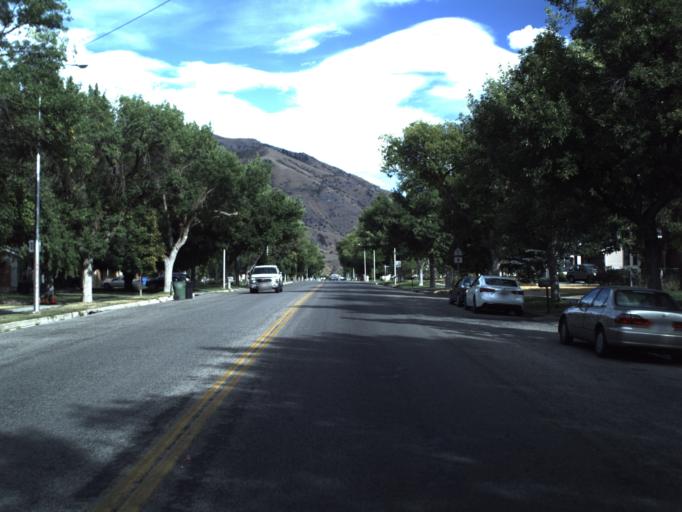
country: US
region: Utah
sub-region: Cache County
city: Hyrum
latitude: 41.6338
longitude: -111.8433
